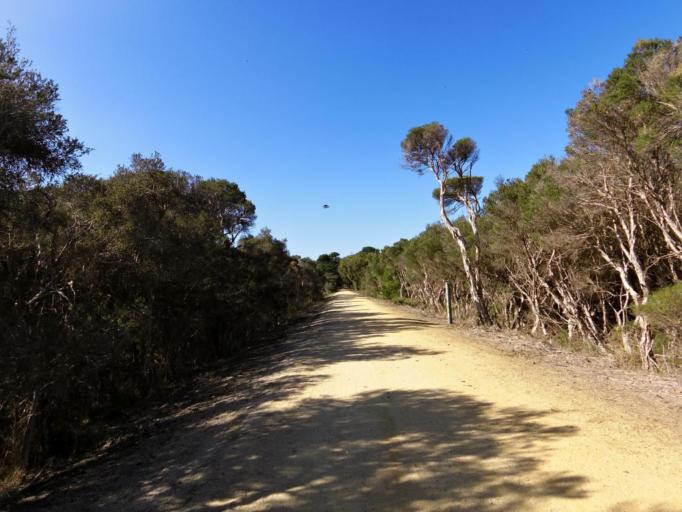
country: AU
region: Victoria
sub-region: Bass Coast
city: North Wonthaggi
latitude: -38.5939
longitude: 145.5637
